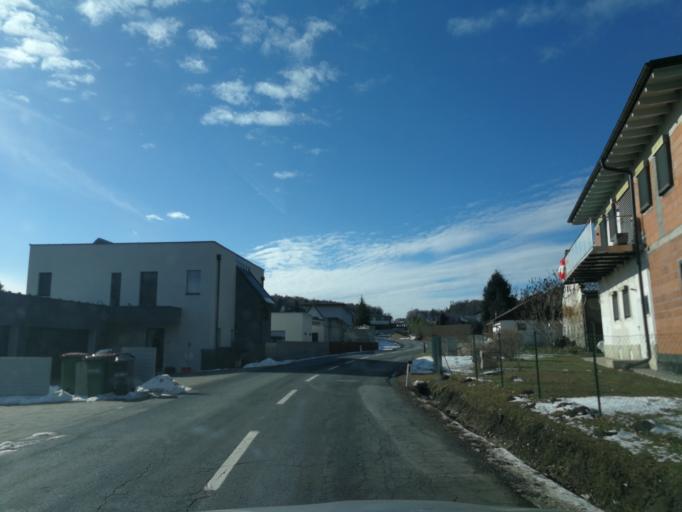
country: AT
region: Styria
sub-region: Politischer Bezirk Graz-Umgebung
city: Langegg bei Graz
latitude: 47.0645
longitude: 15.6328
